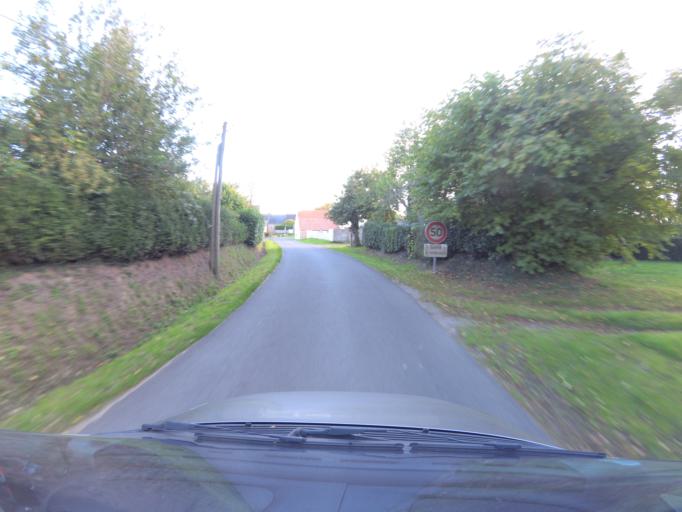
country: FR
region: Brittany
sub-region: Departement du Morbihan
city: Saint-Vincent-sur-Oust
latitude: 47.7149
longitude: -2.1642
